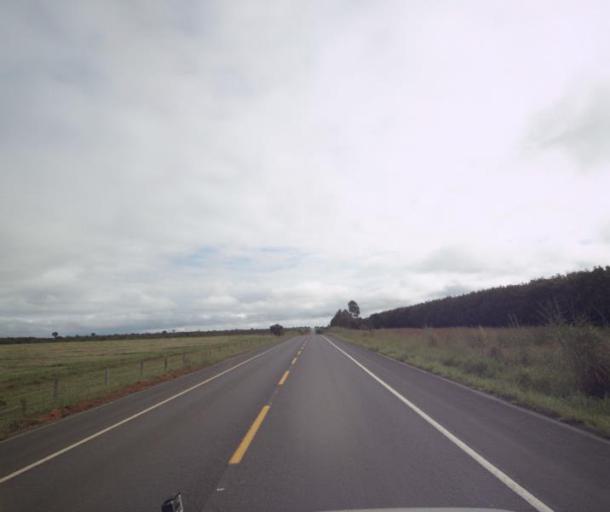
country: BR
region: Goias
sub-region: Padre Bernardo
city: Padre Bernardo
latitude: -15.3732
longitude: -48.6456
